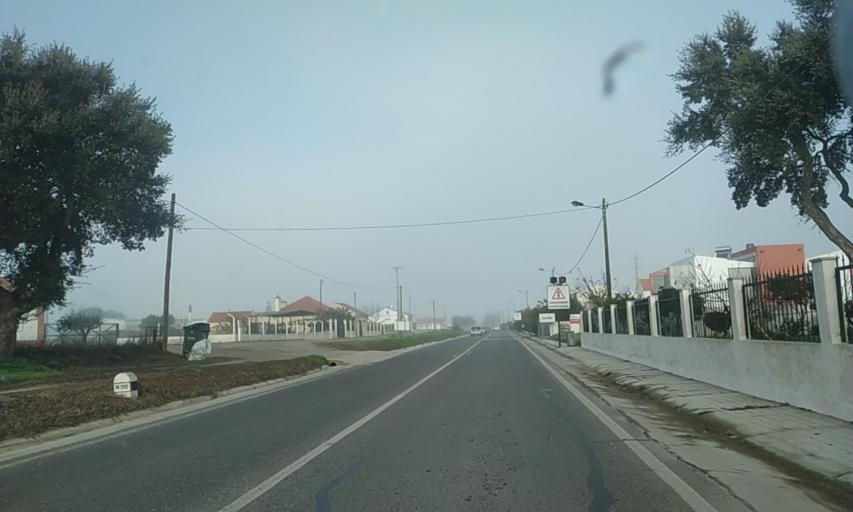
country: PT
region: Setubal
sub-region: Palmela
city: Pinhal Novo
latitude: 38.6624
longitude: -8.9240
